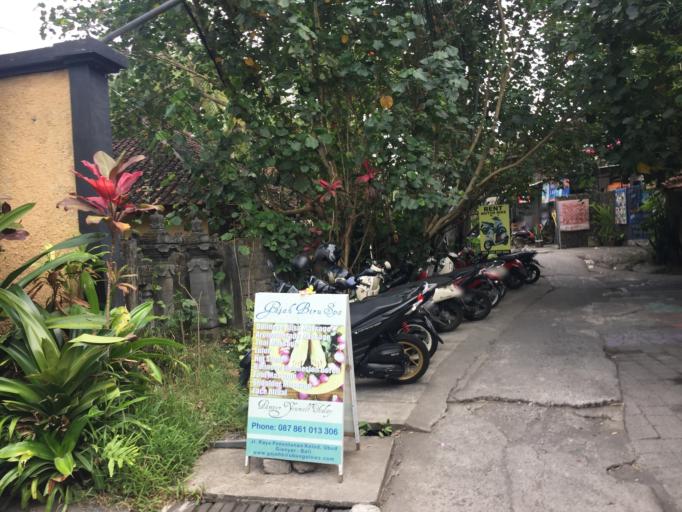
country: ID
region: Bali
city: Banjar Pande
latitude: -8.5068
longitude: 115.2512
